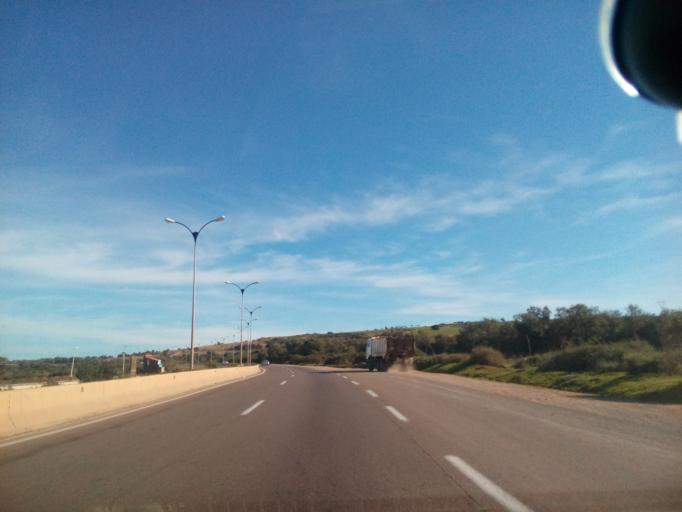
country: DZ
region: Oran
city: Ain el Bya
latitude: 35.7883
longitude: -0.0984
